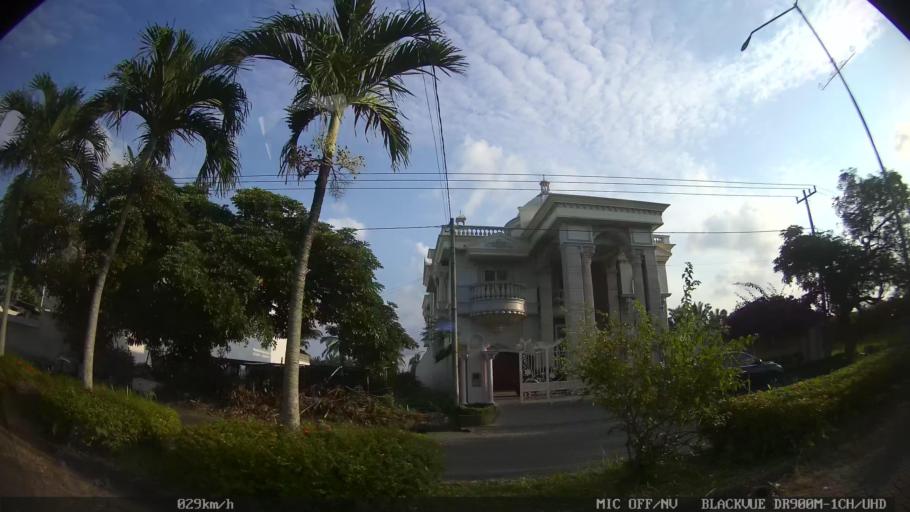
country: ID
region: North Sumatra
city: Medan
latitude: 3.6257
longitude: 98.6433
